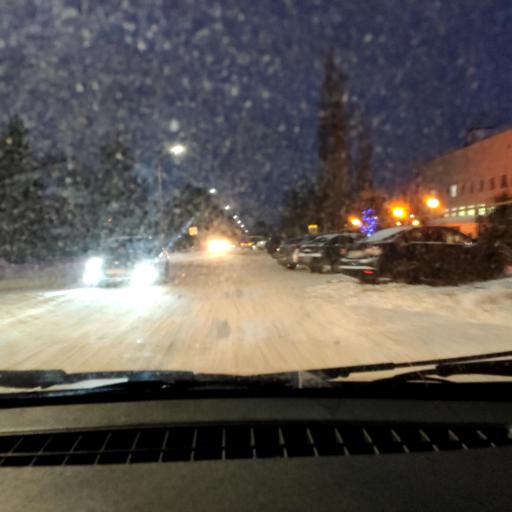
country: RU
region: Bashkortostan
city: Blagoveshchensk
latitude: 55.0471
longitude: 55.9487
